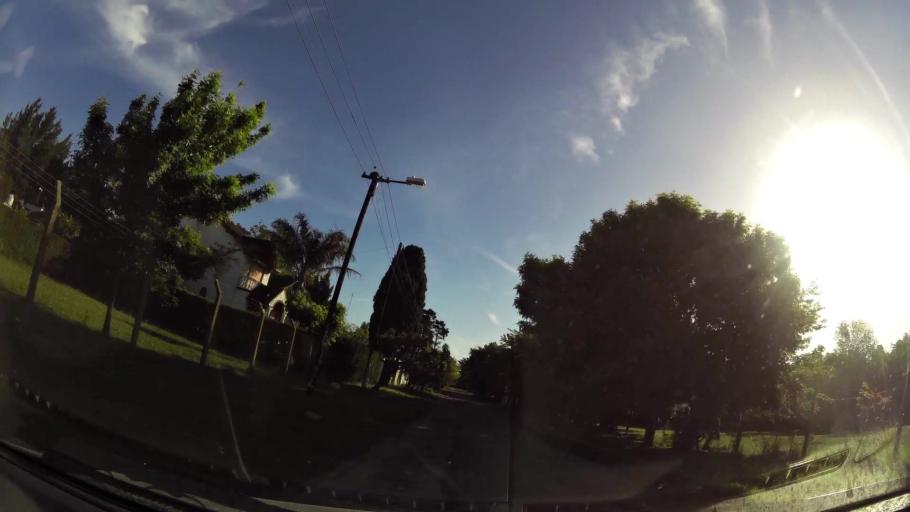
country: AR
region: Buenos Aires
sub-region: Partido de Quilmes
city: Quilmes
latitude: -34.8146
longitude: -58.2152
